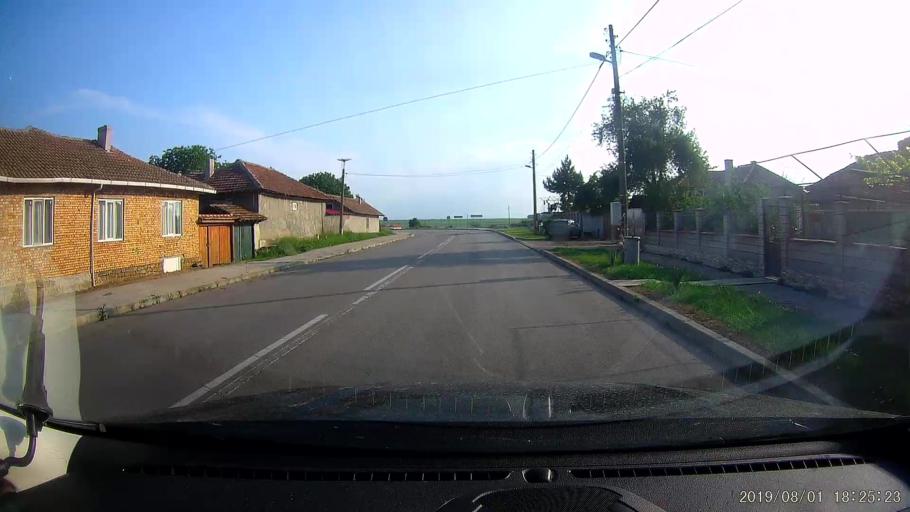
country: BG
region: Shumen
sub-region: Obshtina Venets
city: Venets
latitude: 43.6167
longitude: 26.9963
